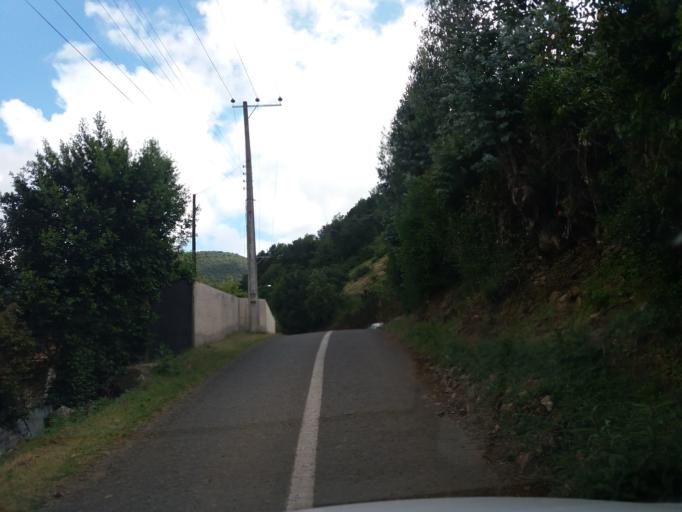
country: CL
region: Valparaiso
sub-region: Provincia de Marga Marga
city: Limache
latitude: -33.0684
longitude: -71.0636
